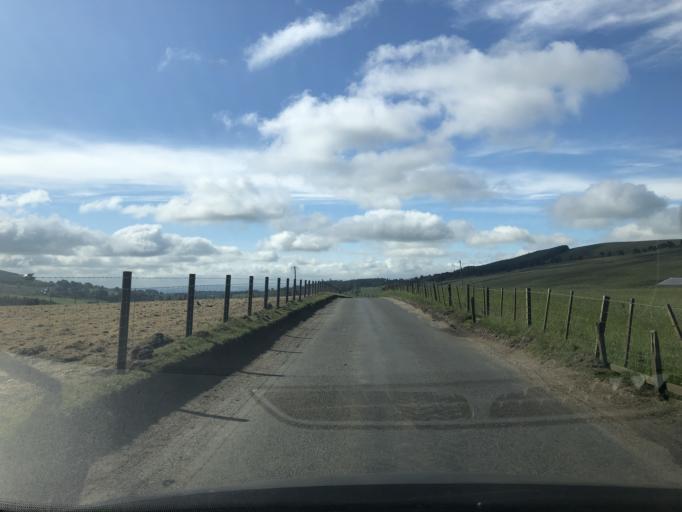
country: GB
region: Scotland
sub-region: Angus
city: Kirriemuir
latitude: 56.7623
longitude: -3.0197
